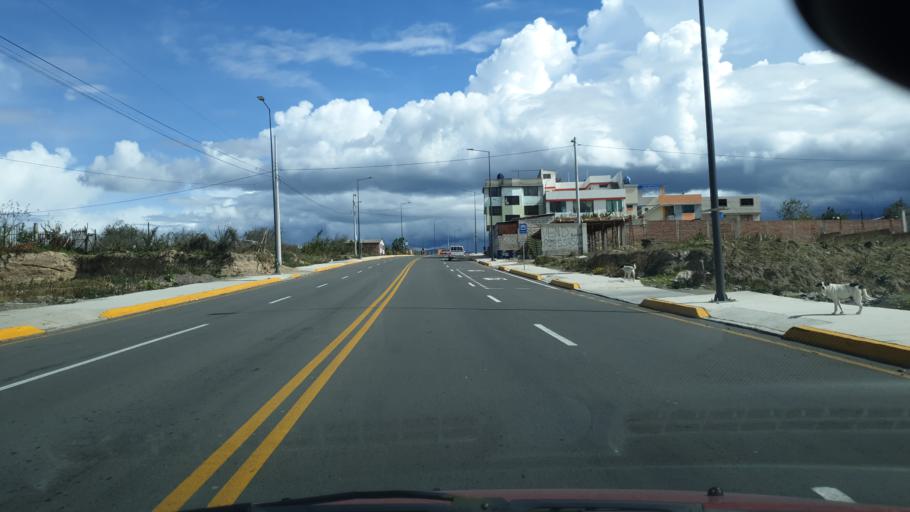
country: EC
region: Tungurahua
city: Ambato
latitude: -1.2955
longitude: -78.6311
